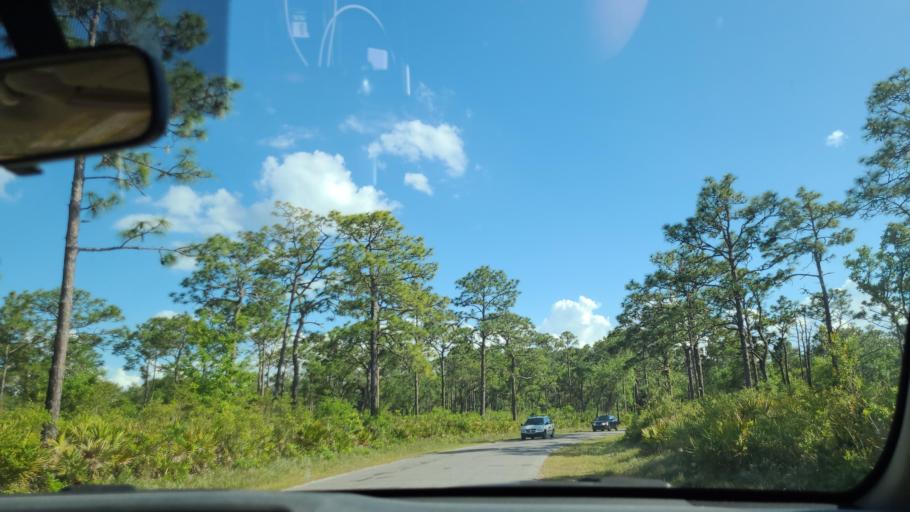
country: US
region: Florida
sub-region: Polk County
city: Babson Park
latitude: 27.9565
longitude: -81.3756
